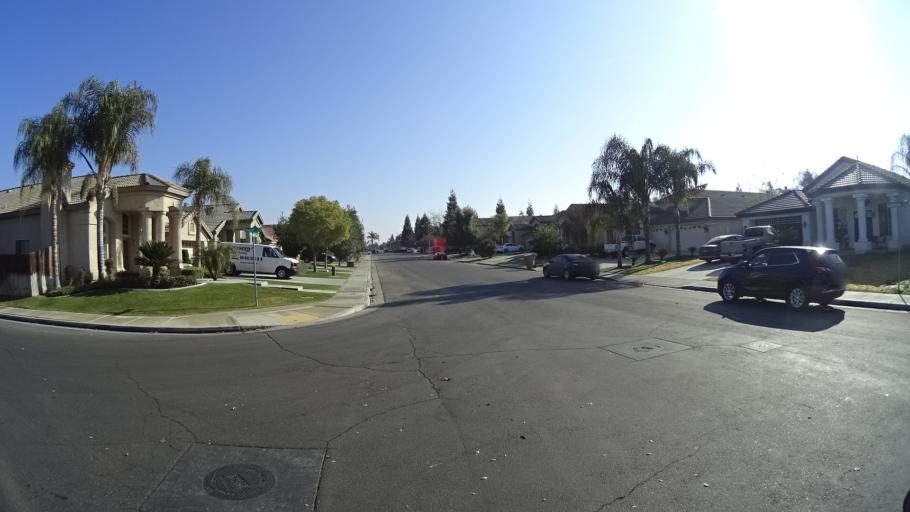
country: US
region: California
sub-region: Kern County
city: Greenacres
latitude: 35.3082
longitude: -119.1145
